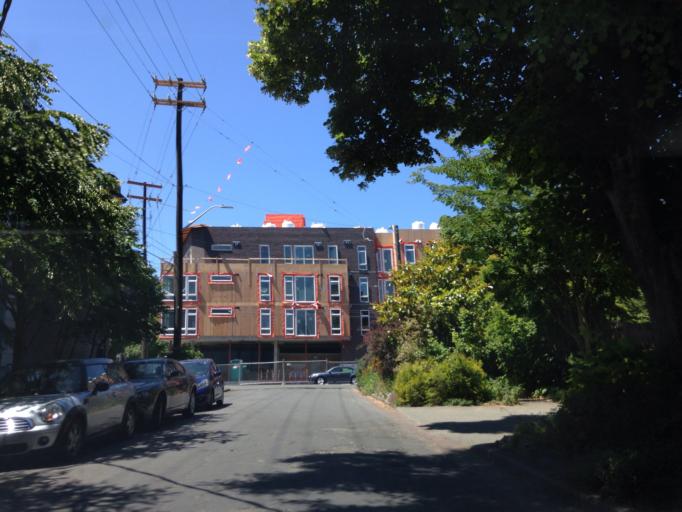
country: US
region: Washington
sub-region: King County
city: Seattle
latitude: 47.6245
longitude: -122.3120
